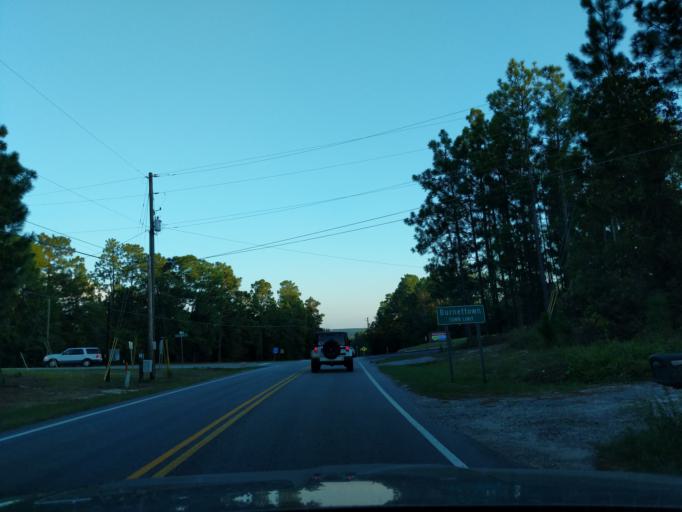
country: US
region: South Carolina
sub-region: Aiken County
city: Burnettown
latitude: 33.5350
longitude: -81.8619
